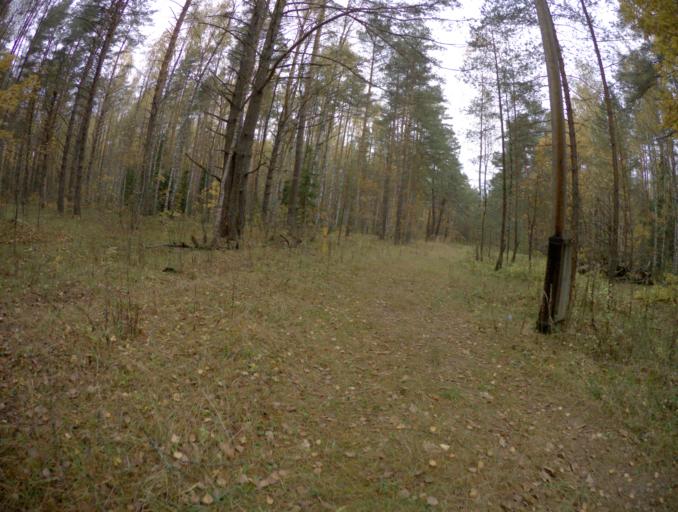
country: RU
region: Vladimir
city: Kommunar
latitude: 56.0757
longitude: 40.4442
